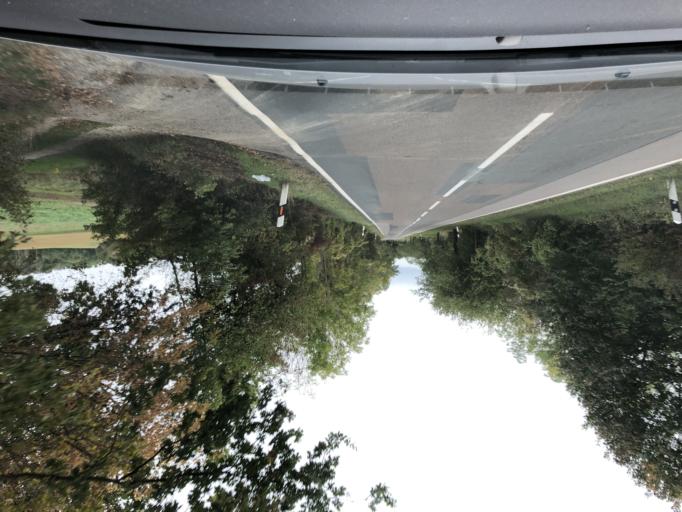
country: DE
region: Saxony-Anhalt
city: Bad Kosen
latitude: 51.1555
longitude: 11.7503
